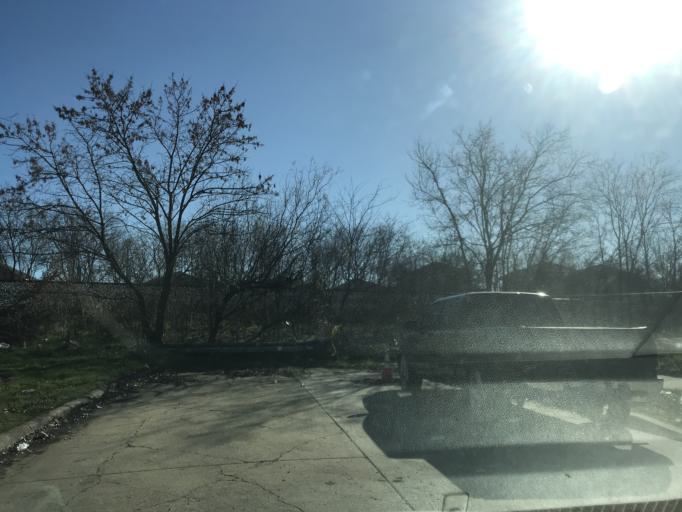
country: US
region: Texas
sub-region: Dallas County
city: Cockrell Hill
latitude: 32.7697
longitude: -96.9089
